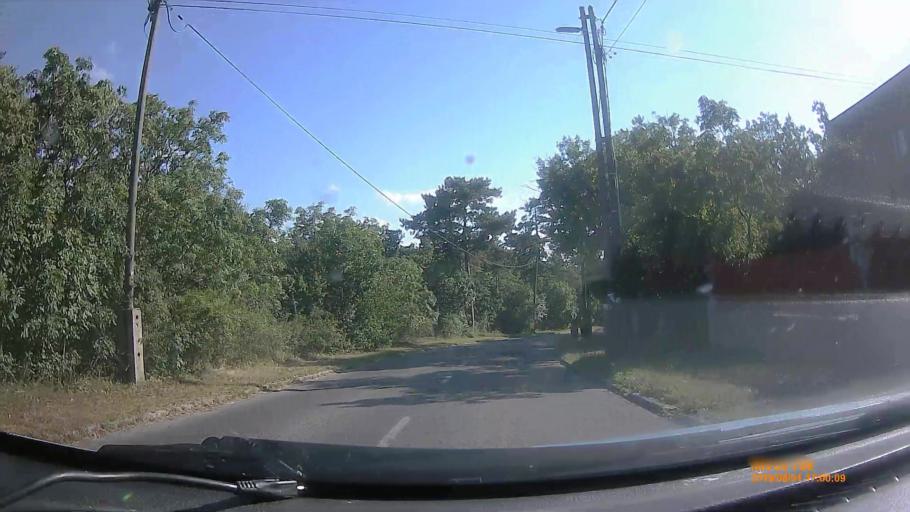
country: HU
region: Baranya
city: Pecs
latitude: 46.0899
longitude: 18.2291
